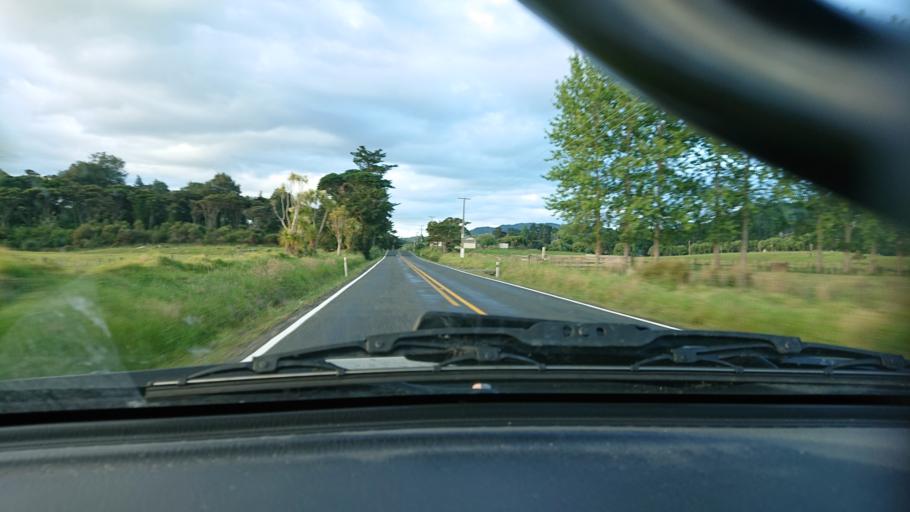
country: NZ
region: Auckland
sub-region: Auckland
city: Parakai
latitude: -36.4943
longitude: 174.4484
